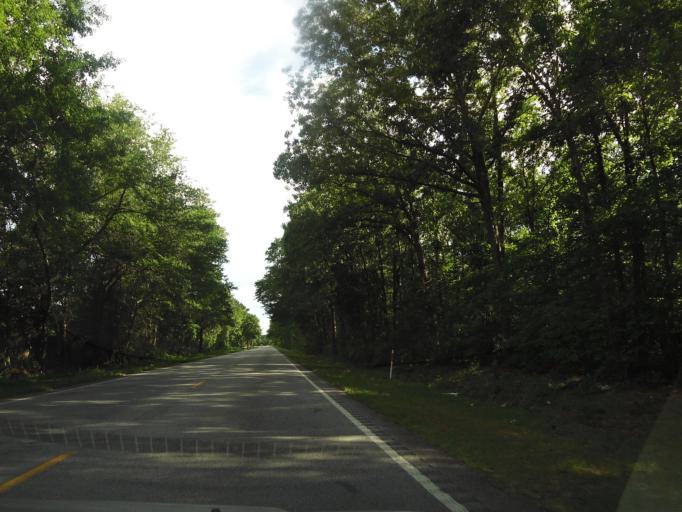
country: US
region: South Carolina
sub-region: Hampton County
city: Estill
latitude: 32.8489
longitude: -81.2387
